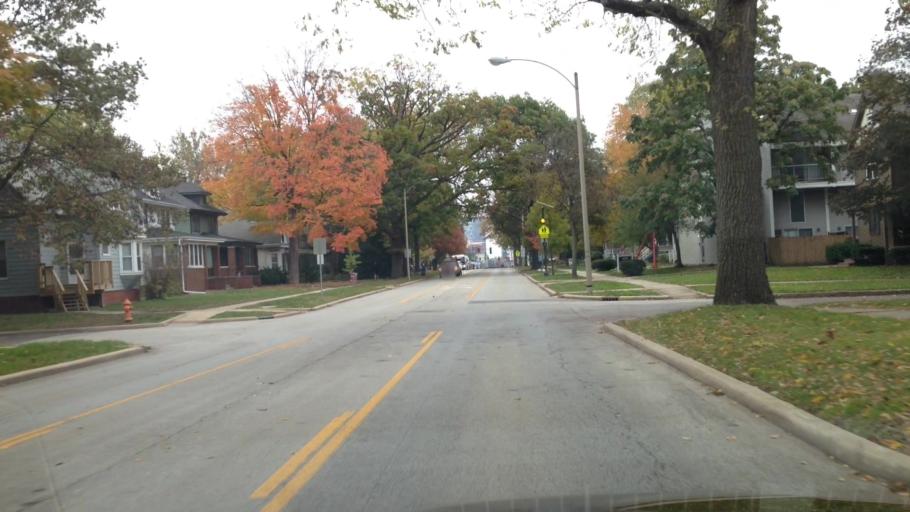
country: US
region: Illinois
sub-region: Champaign County
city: Champaign
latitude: 40.1101
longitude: -88.2504
